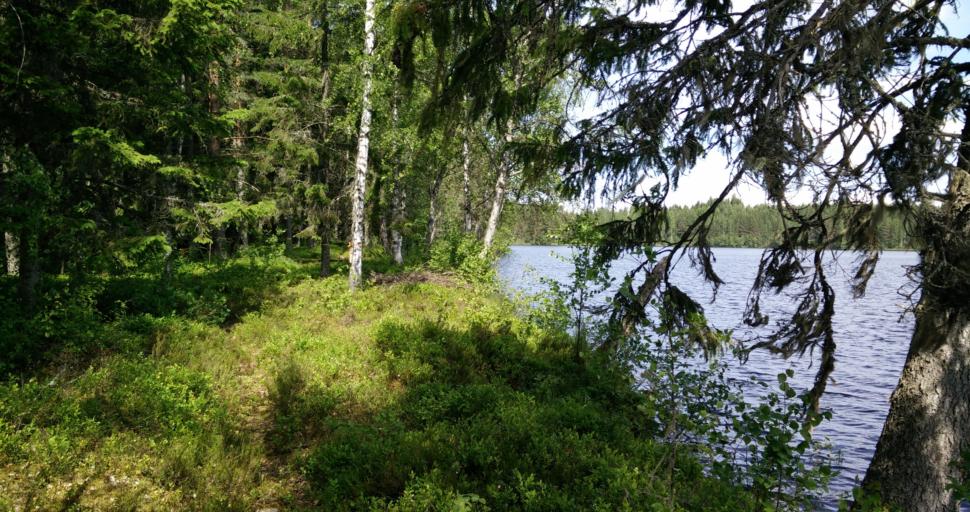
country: SE
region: Vaermland
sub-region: Hagfors Kommun
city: Hagfors
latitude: 59.9940
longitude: 13.5725
